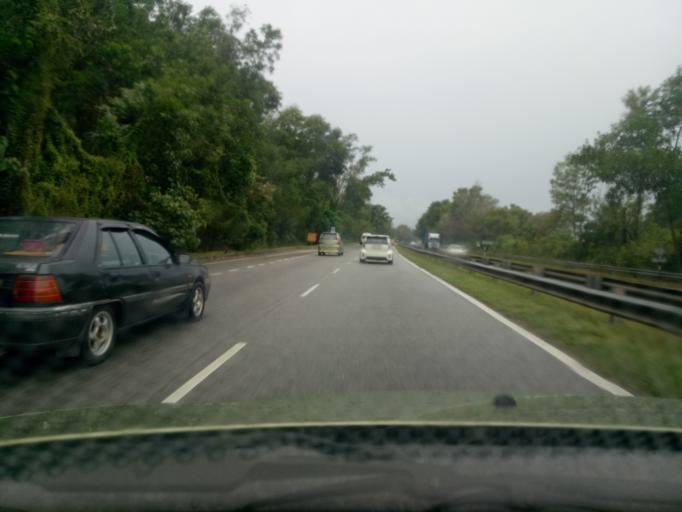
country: MY
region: Kedah
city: Sungai Petani
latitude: 5.6457
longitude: 100.5391
